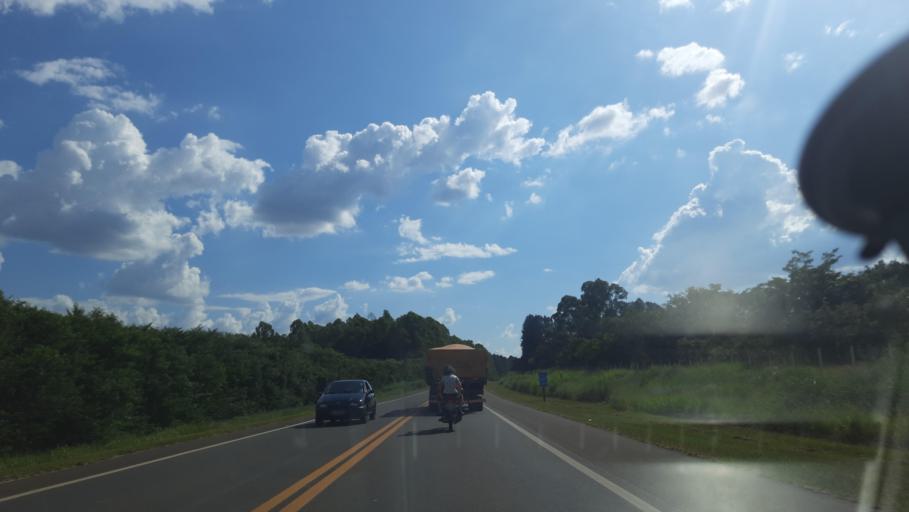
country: BR
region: Sao Paulo
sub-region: Casa Branca
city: Casa Branca
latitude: -21.7556
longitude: -47.0022
